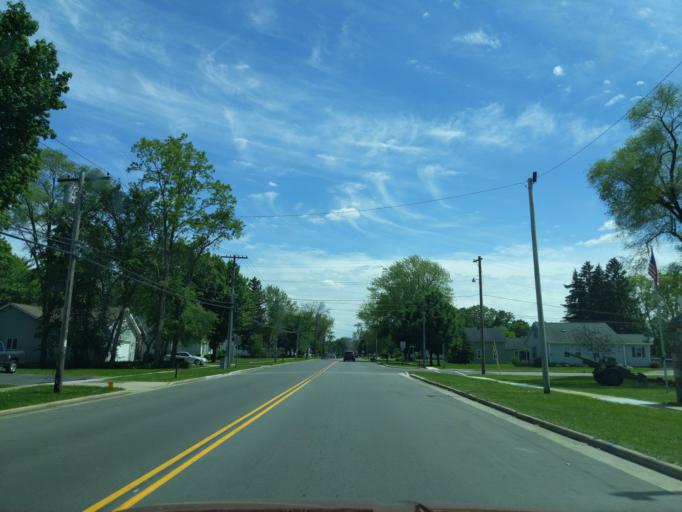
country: US
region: Wisconsin
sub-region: Columbia County
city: Pardeeville
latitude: 43.5426
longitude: -89.3018
